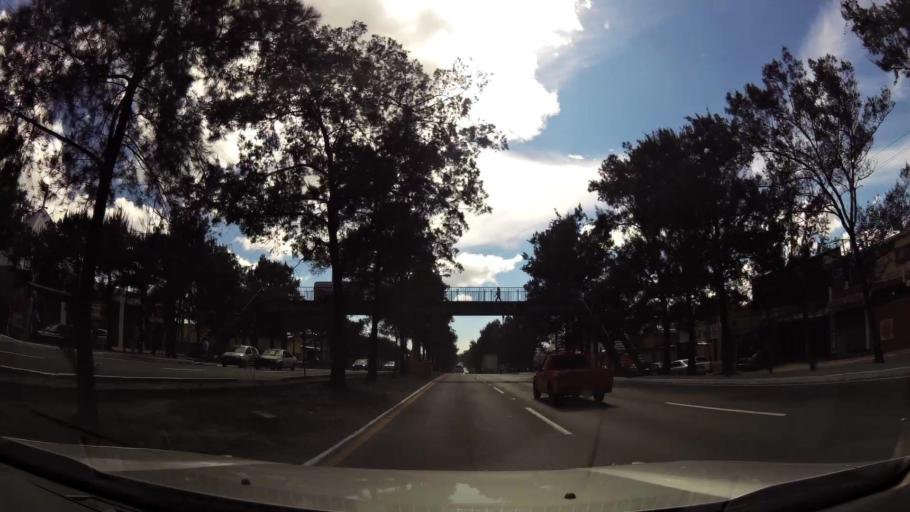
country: GT
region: Guatemala
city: Guatemala City
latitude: 14.6382
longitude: -90.5508
